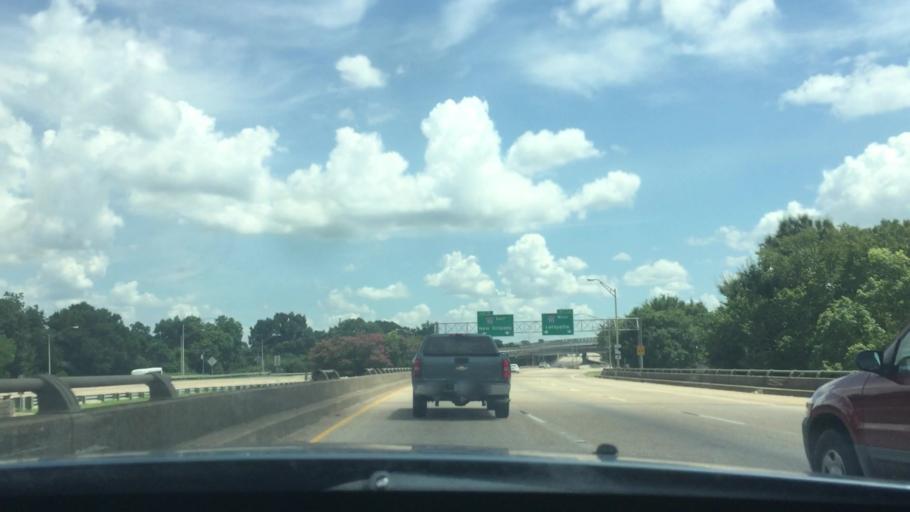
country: US
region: Louisiana
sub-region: East Baton Rouge Parish
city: Baton Rouge
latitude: 30.4433
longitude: -91.1782
